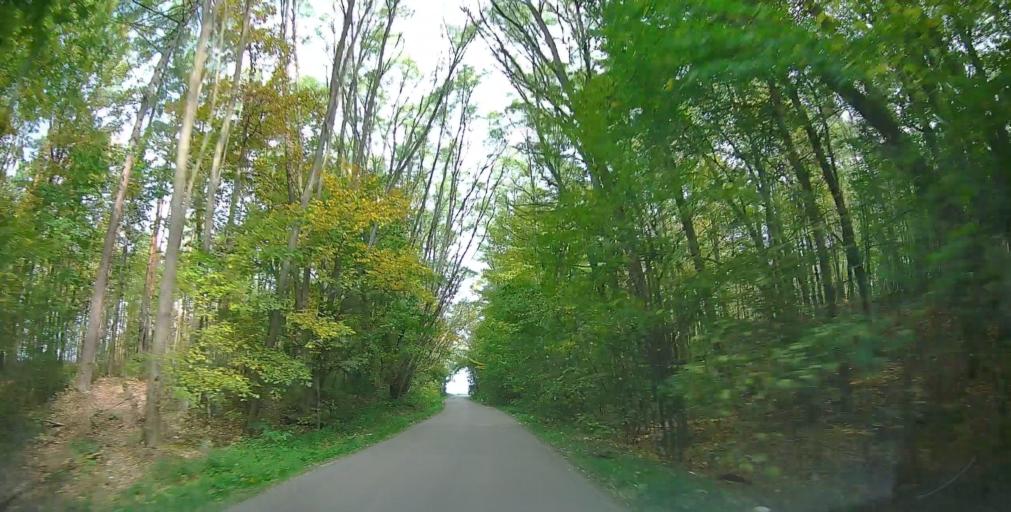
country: PL
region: Masovian Voivodeship
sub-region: Powiat grojecki
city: Mogielnica
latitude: 51.6446
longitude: 20.7547
